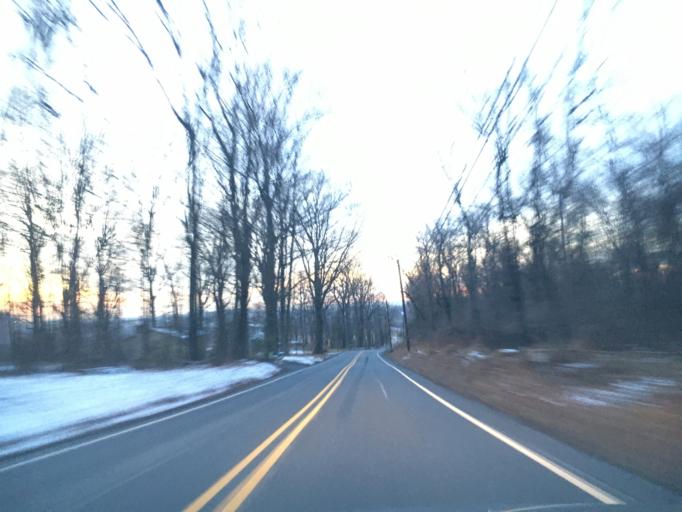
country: US
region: Pennsylvania
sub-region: Northampton County
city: Youngsville
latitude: 40.7636
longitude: -75.4433
